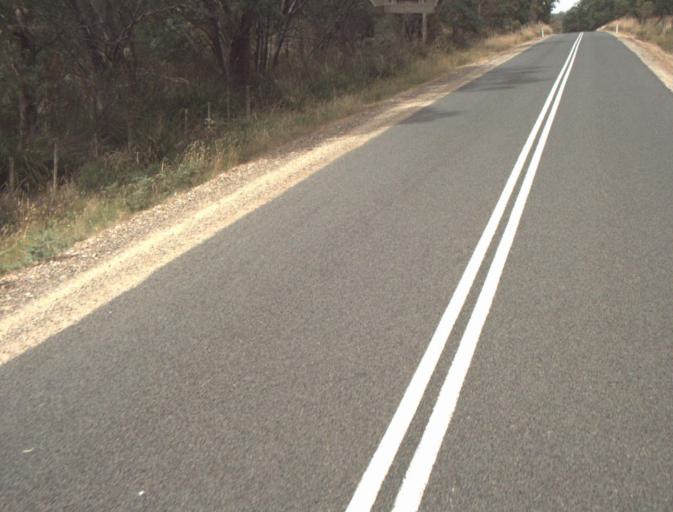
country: AU
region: Tasmania
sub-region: Northern Midlands
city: Evandale
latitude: -41.5105
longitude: 147.3318
